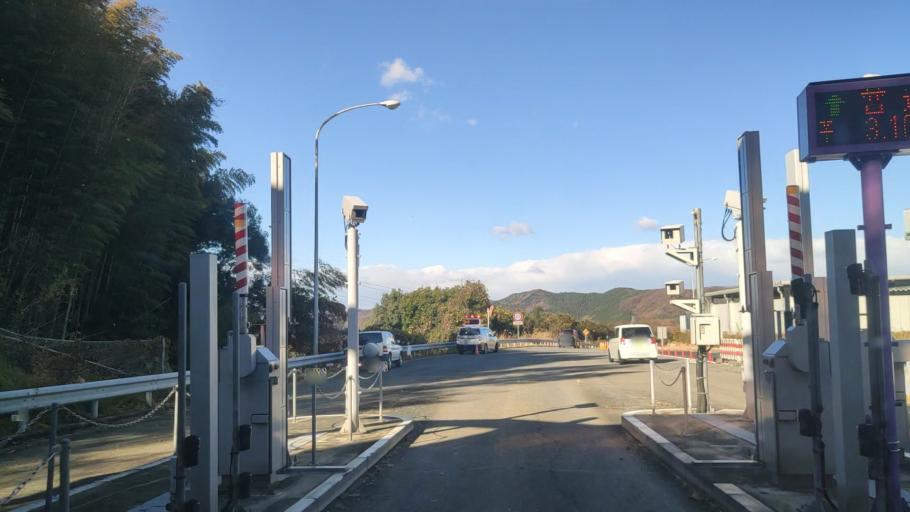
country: JP
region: Ehime
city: Saijo
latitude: 33.9145
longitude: 133.2369
